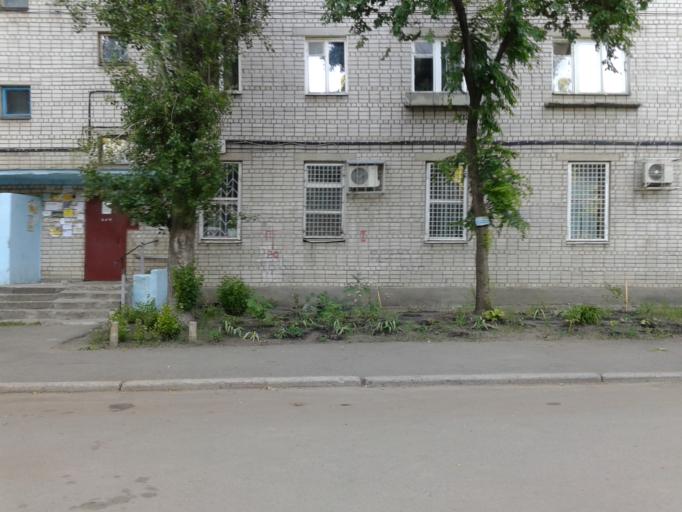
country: RU
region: Voronezj
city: Pridonskoy
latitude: 51.6568
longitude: 39.1166
